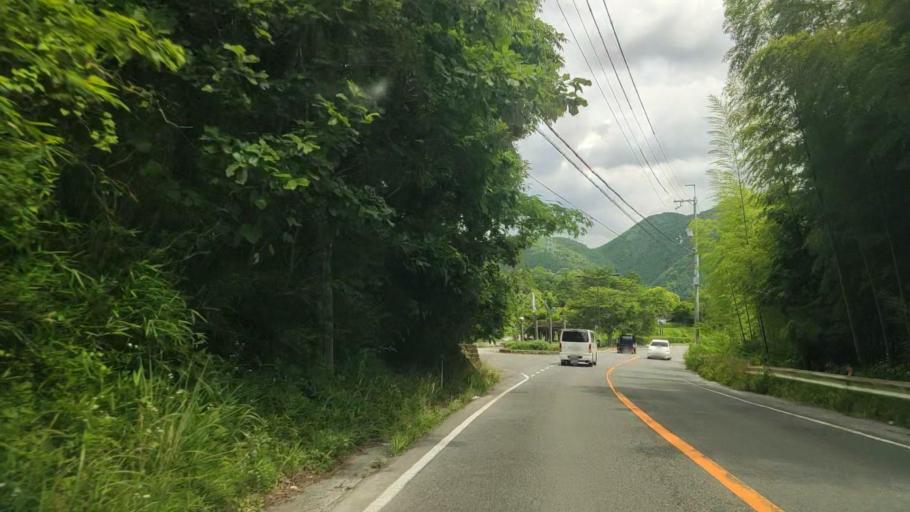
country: JP
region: Hyogo
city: Yamazakicho-nakabirose
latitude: 34.9868
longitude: 134.4127
